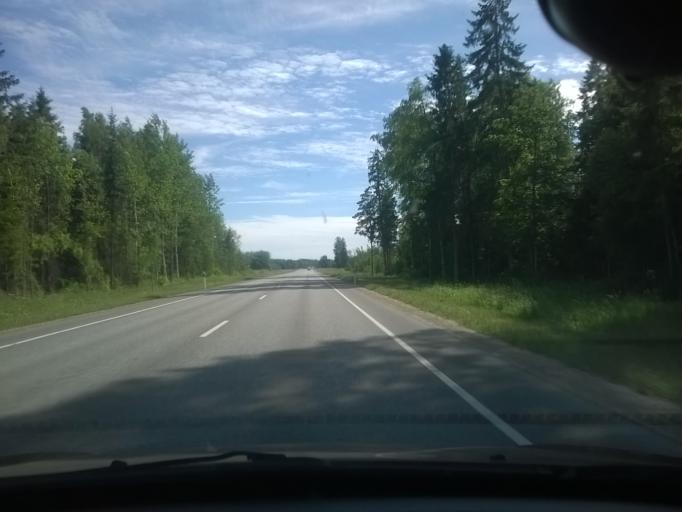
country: EE
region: Jaervamaa
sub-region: Paide linn
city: Paide
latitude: 58.9474
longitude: 25.6462
